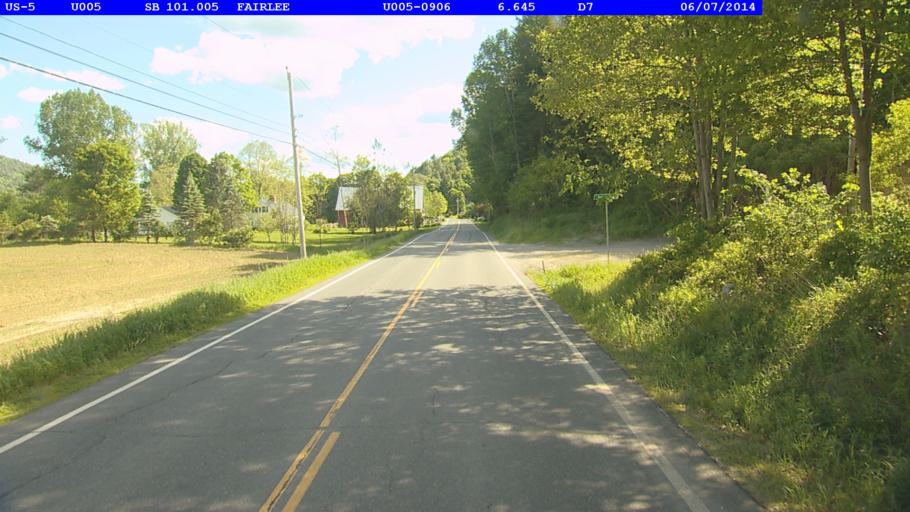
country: US
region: New Hampshire
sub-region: Grafton County
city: Orford
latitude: 43.9523
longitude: -72.1166
